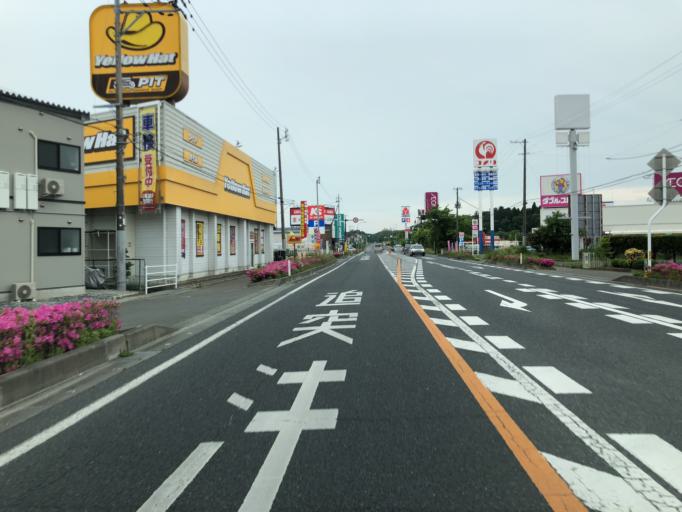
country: JP
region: Miyagi
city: Marumori
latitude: 37.7892
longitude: 140.9311
